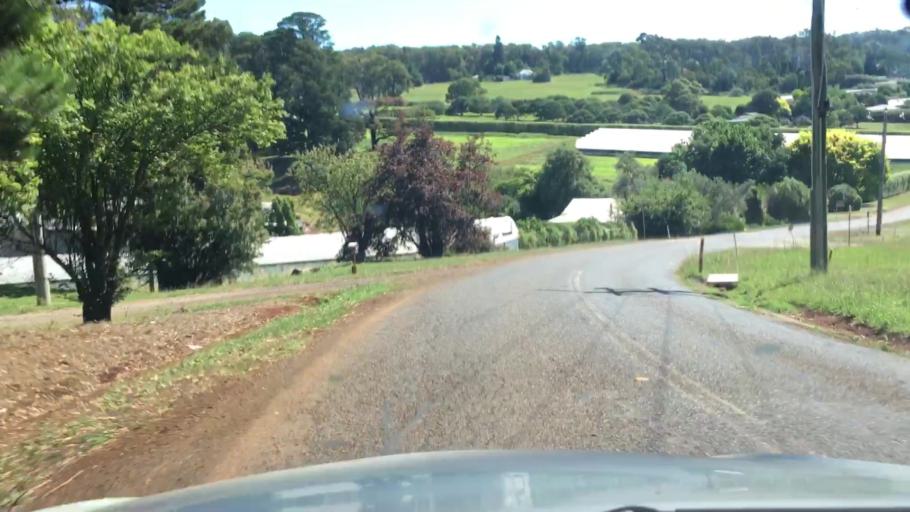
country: AU
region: Victoria
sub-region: Yarra Ranges
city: Mount Evelyn
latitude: -37.8189
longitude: 145.4221
